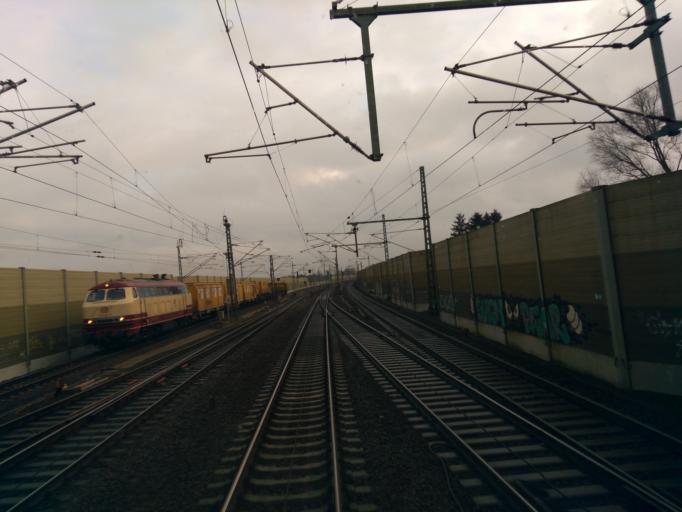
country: DE
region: Lower Saxony
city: Stelle
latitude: 53.3853
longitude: 10.1135
